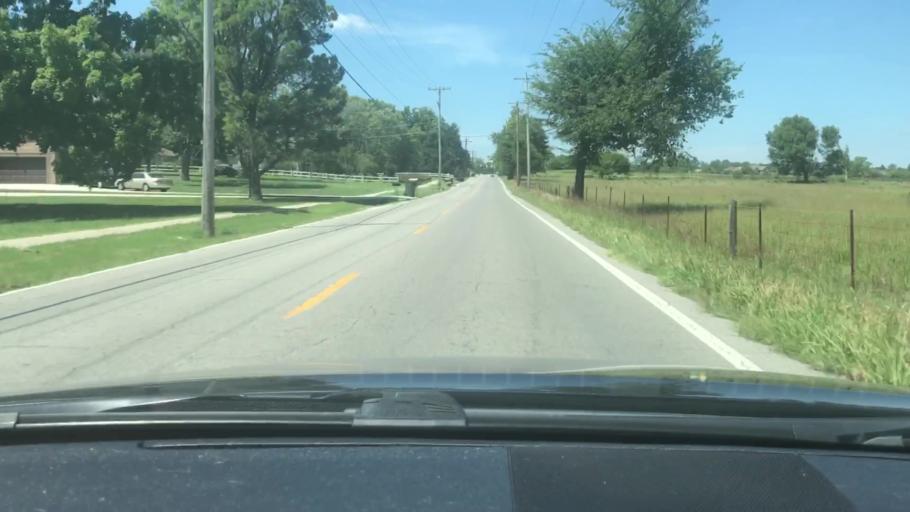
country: US
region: Tennessee
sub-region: Sumner County
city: Gallatin
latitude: 36.3964
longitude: -86.4739
